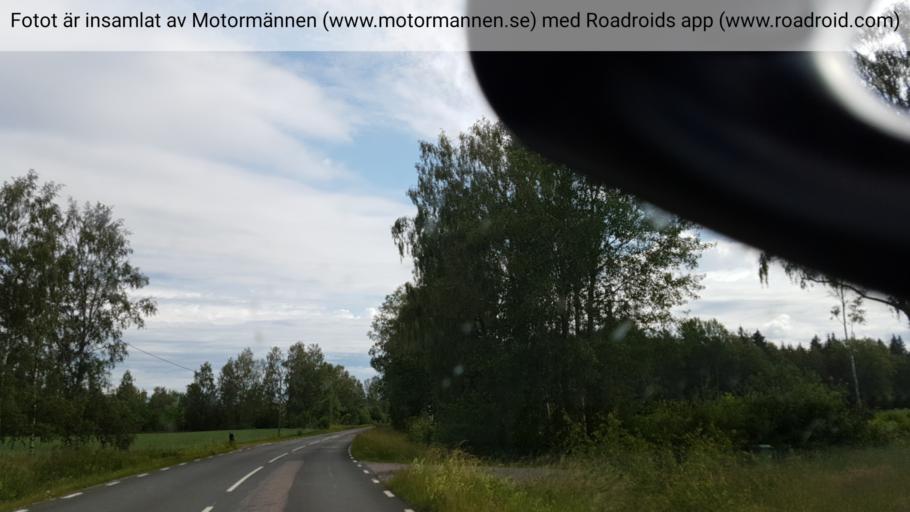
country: SE
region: Vaestra Goetaland
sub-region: Falkopings Kommun
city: Floby
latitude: 58.2070
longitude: 13.3693
